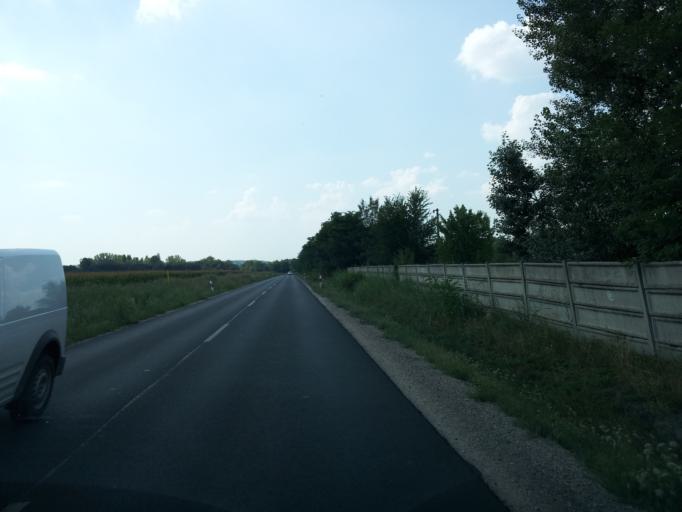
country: HU
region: Pest
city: Toekoel
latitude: 47.3380
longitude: 18.9781
